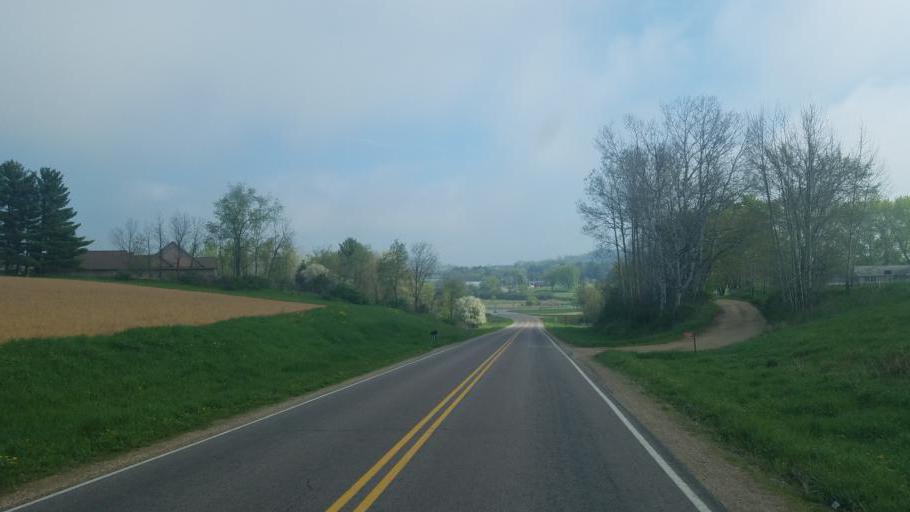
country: US
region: Wisconsin
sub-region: Vernon County
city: Hillsboro
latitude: 43.6455
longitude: -90.3522
